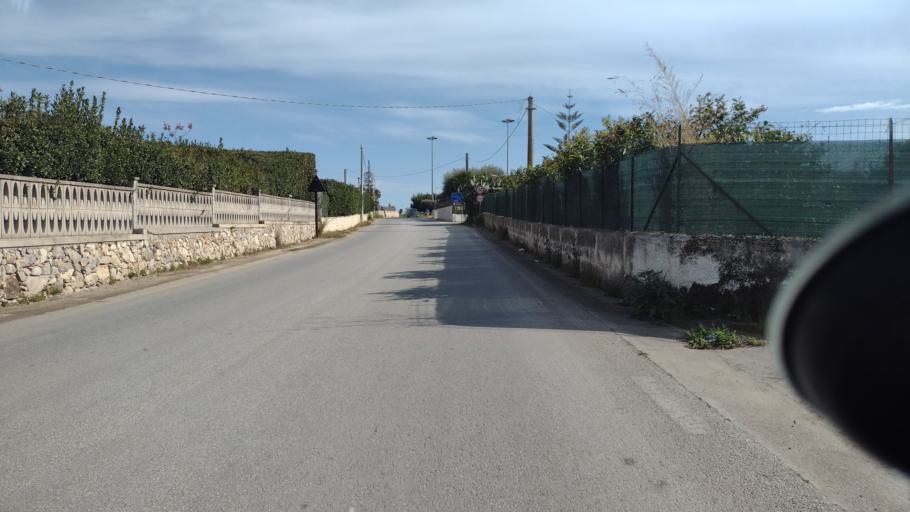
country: IT
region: Sicily
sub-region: Provincia di Siracusa
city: Avola
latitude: 36.8726
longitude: 15.1270
